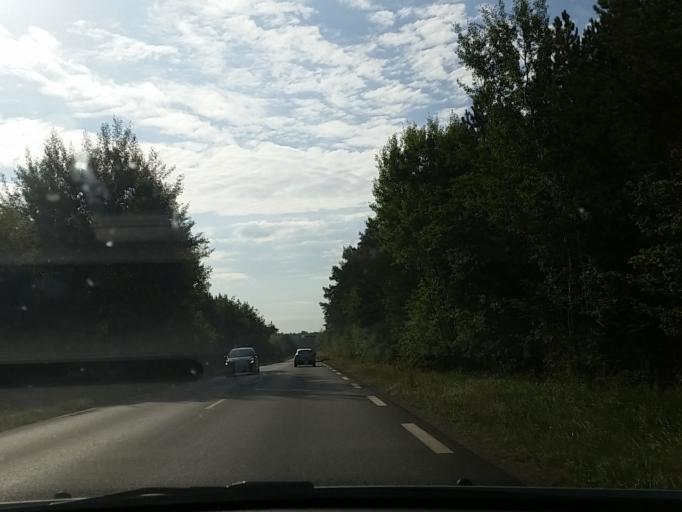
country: FR
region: Centre
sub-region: Departement du Loir-et-Cher
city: Mur-de-Sologne
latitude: 47.4025
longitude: 1.6313
